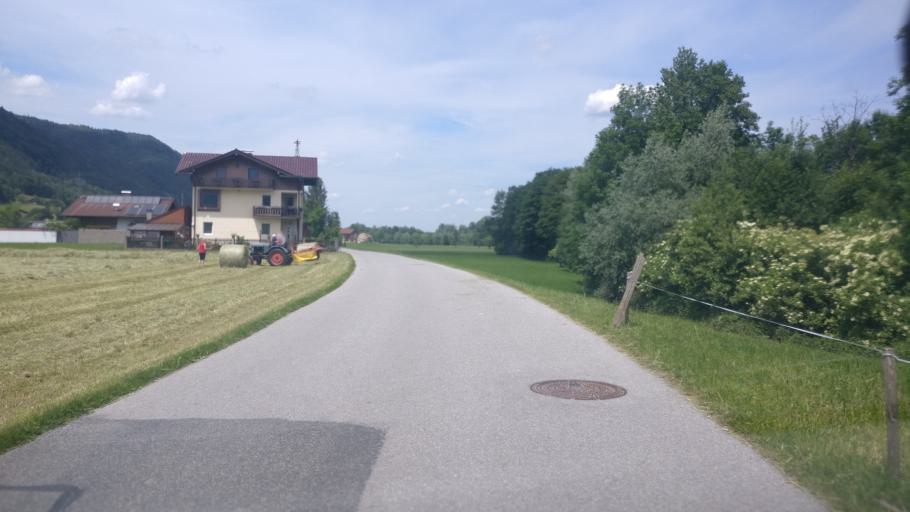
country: AT
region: Salzburg
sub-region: Politischer Bezirk Hallein
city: Kuchl
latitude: 47.6268
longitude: 13.1376
